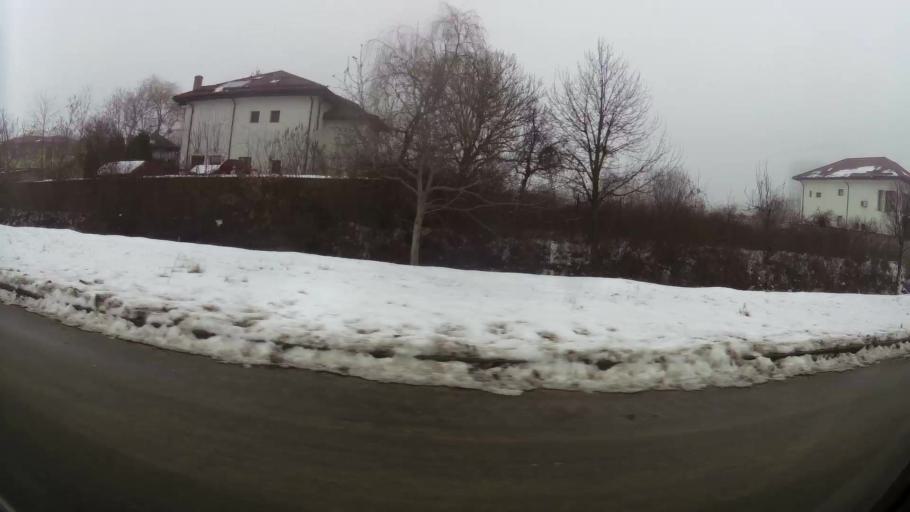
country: RO
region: Ilfov
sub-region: Comuna Chiajna
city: Rosu
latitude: 44.4474
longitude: 26.0193
